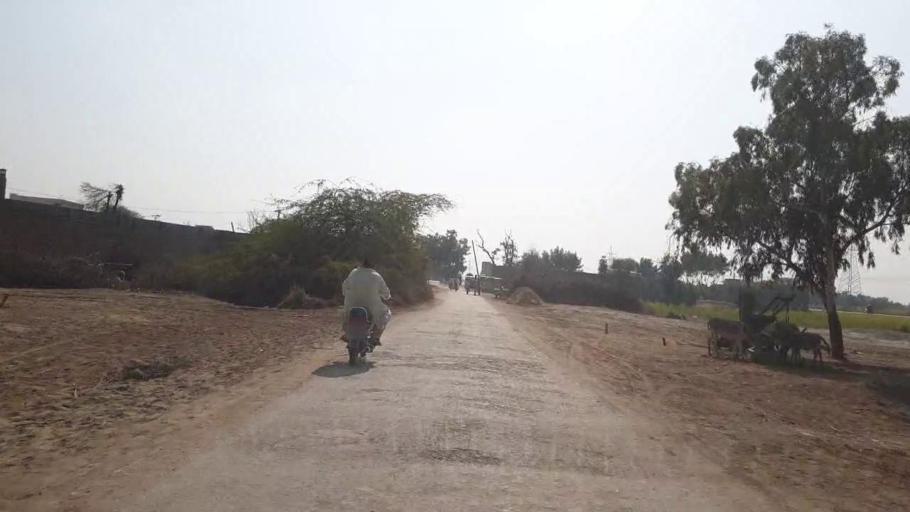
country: PK
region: Sindh
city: Bhit Shah
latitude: 25.6969
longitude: 68.5432
